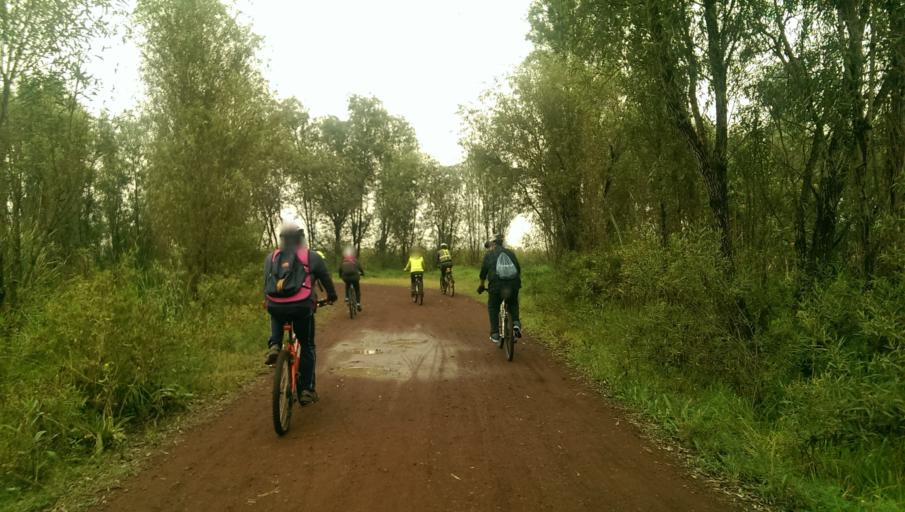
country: MX
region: Mexico City
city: Xochimilco
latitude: 19.2726
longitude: -99.0742
